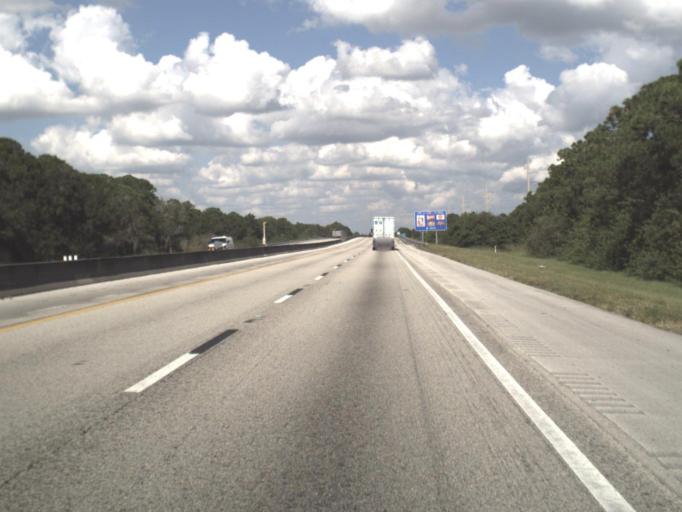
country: US
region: Florida
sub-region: Saint Lucie County
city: Port Saint Lucie
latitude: 27.2393
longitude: -80.3448
